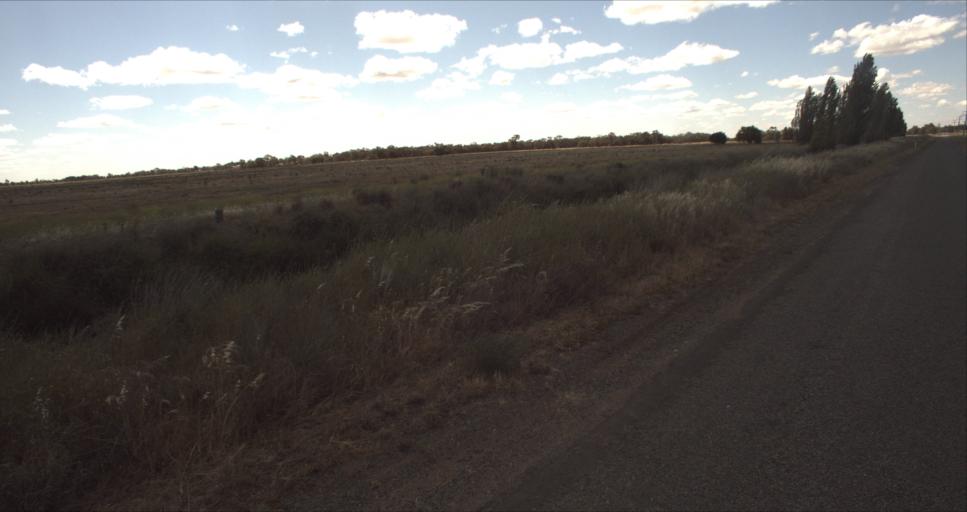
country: AU
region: New South Wales
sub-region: Leeton
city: Leeton
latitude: -34.5287
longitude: 146.2195
